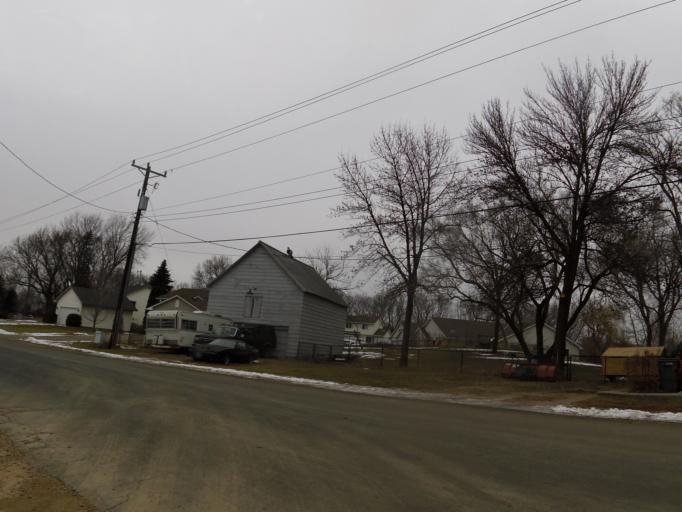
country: US
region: Minnesota
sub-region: Carver County
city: Cologne
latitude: 44.7758
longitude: -93.7804
